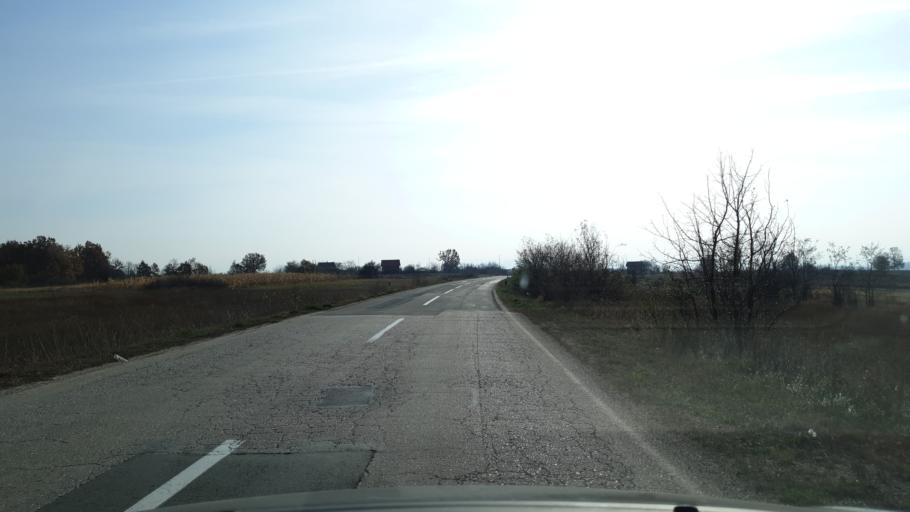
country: RS
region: Central Serbia
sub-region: Borski Okrug
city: Bor
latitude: 43.9909
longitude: 22.0729
